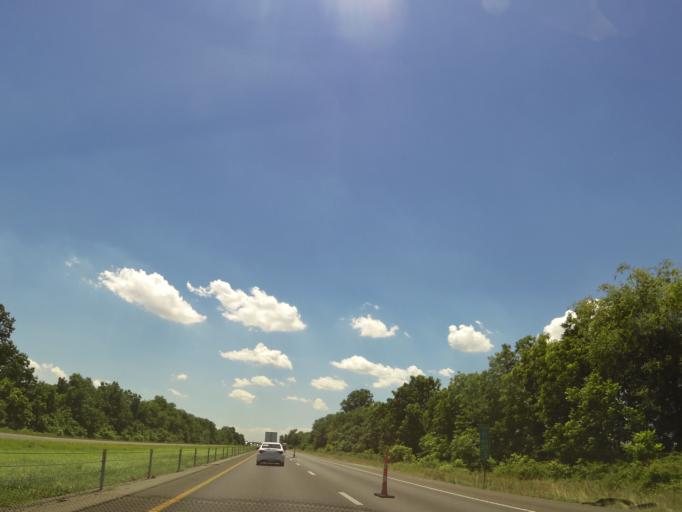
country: US
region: Missouri
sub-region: New Madrid County
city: Portageville
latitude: 36.4500
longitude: -89.6642
